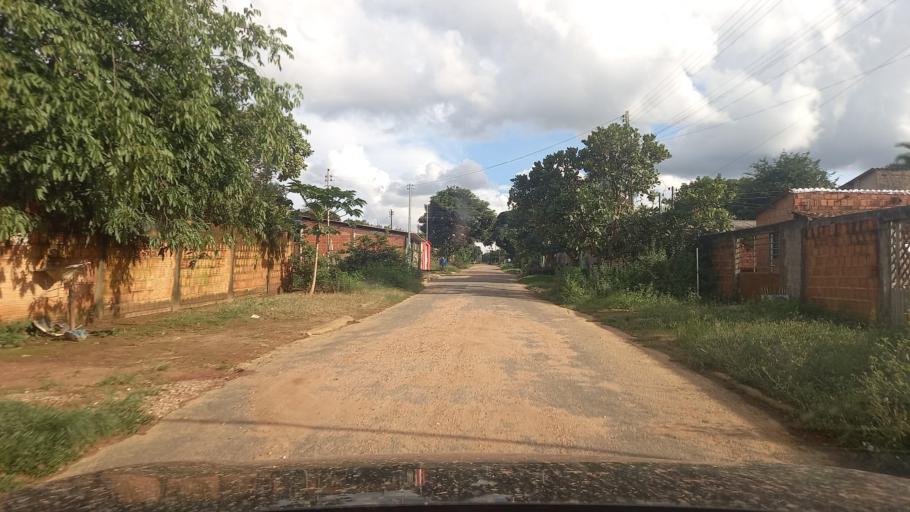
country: BR
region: Goias
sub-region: Cavalcante
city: Cavalcante
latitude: -13.7953
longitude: -47.4445
